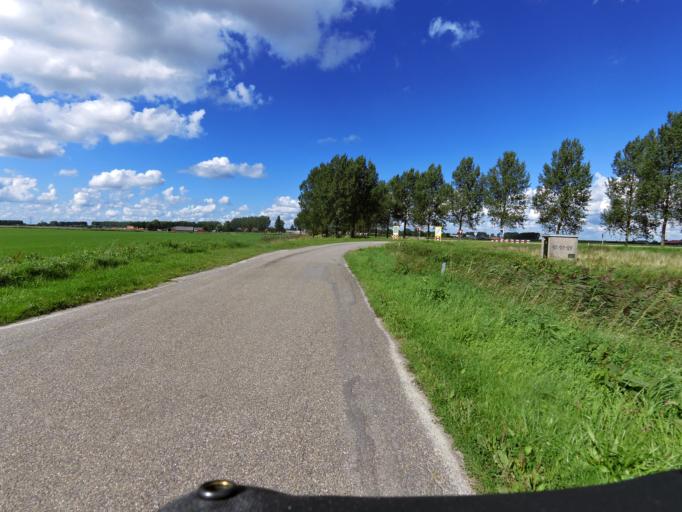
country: NL
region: South Holland
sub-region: Gemeente Goeree-Overflakkee
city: Middelharnis
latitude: 51.7264
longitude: 4.2412
